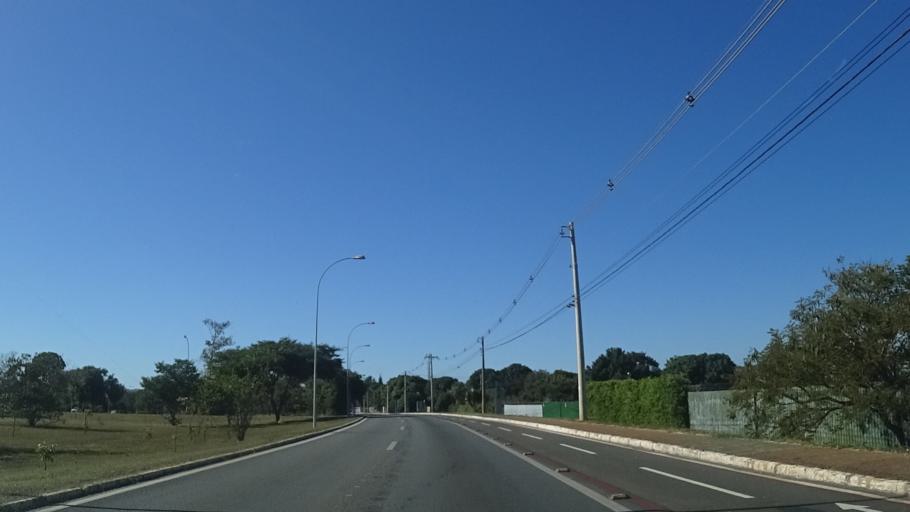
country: BR
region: Federal District
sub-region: Brasilia
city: Brasilia
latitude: -15.7402
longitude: -47.8579
